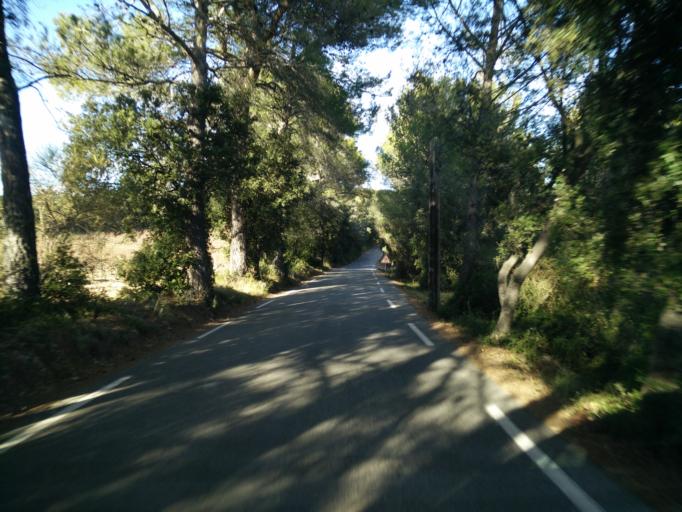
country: FR
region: Provence-Alpes-Cote d'Azur
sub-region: Departement du Var
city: Taradeau
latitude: 43.4642
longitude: 6.4323
